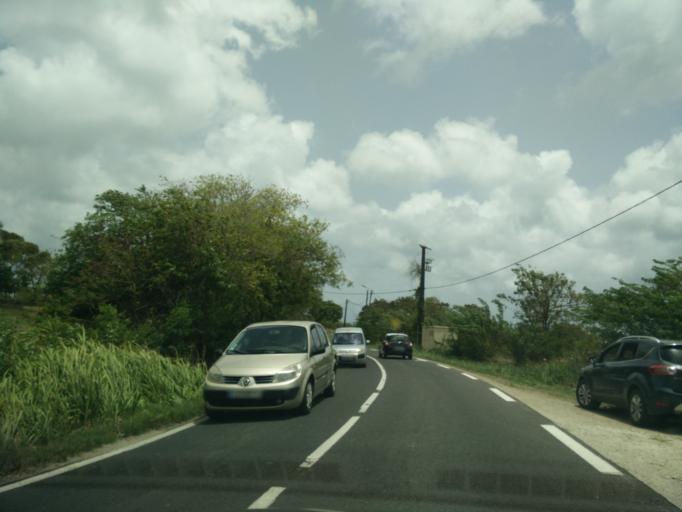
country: GP
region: Guadeloupe
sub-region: Guadeloupe
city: Port-Louis
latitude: 16.4109
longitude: -61.5172
